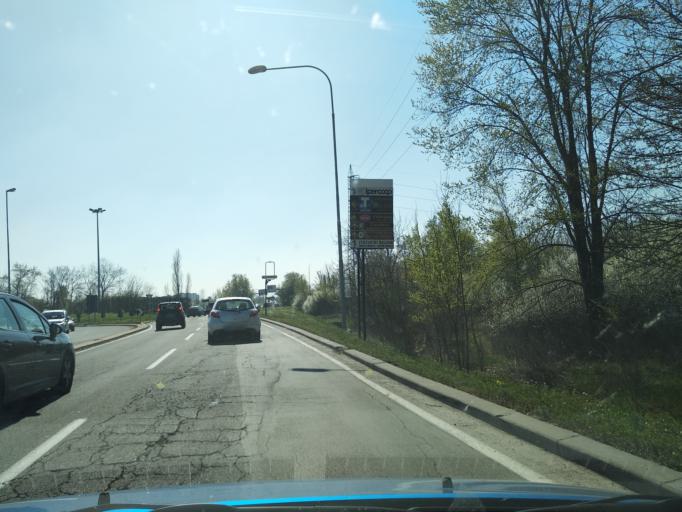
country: IT
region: Emilia-Romagna
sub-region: Provincia di Reggio Emilia
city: Reggio nell'Emilia
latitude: 44.6935
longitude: 10.6092
